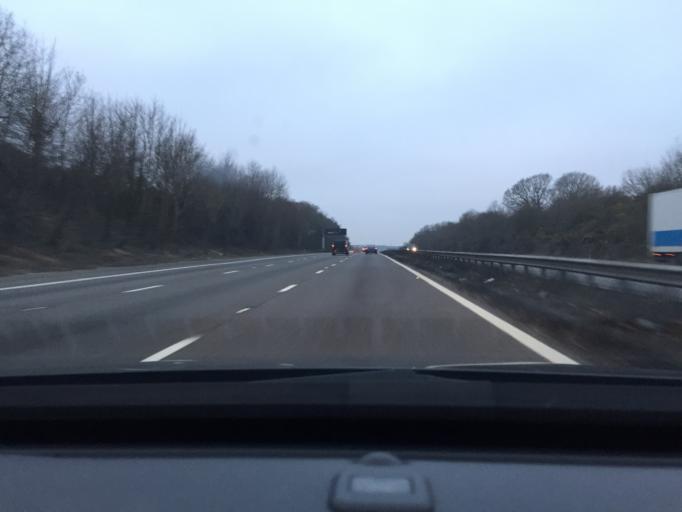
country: GB
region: England
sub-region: Hampshire
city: Fareham
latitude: 50.8679
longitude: -1.2069
